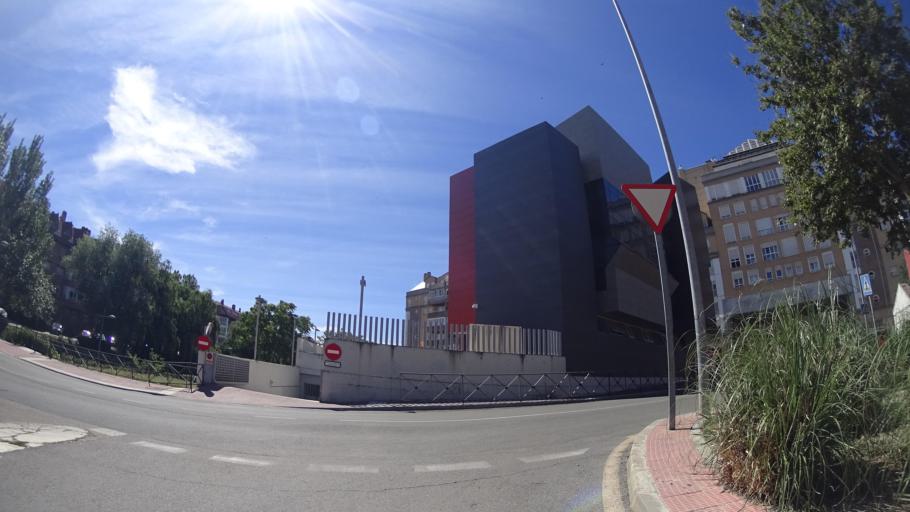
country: ES
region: Madrid
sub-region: Provincia de Madrid
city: Collado-Villalba
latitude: 40.6276
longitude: -4.0056
